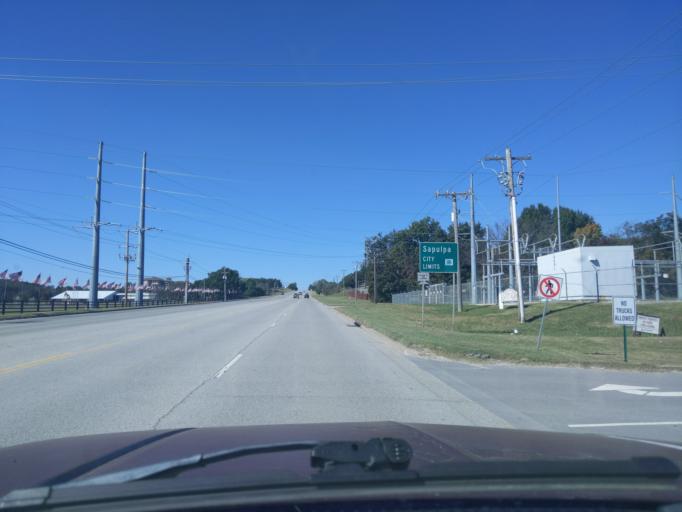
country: US
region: Oklahoma
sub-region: Tulsa County
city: Glenpool
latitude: 35.9884
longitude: -96.0338
